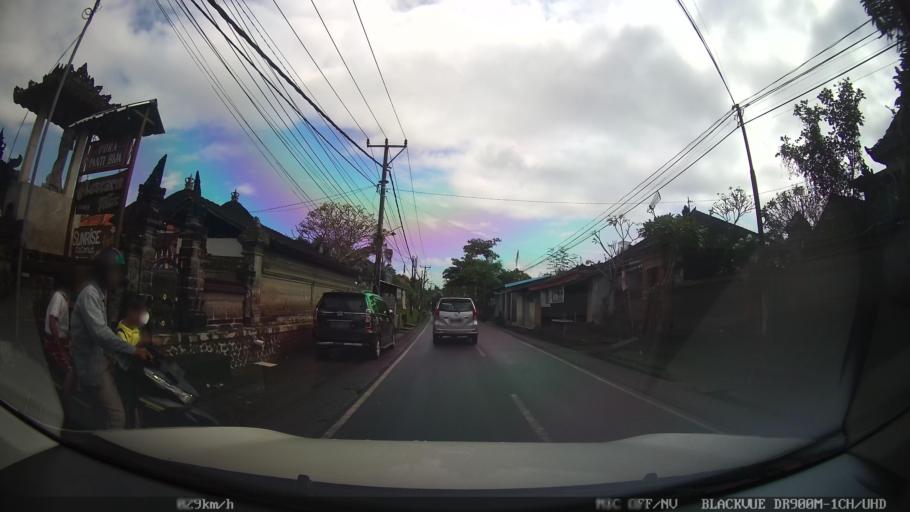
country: ID
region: Bali
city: Banjar Tebongkang
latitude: -8.5428
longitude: 115.2591
